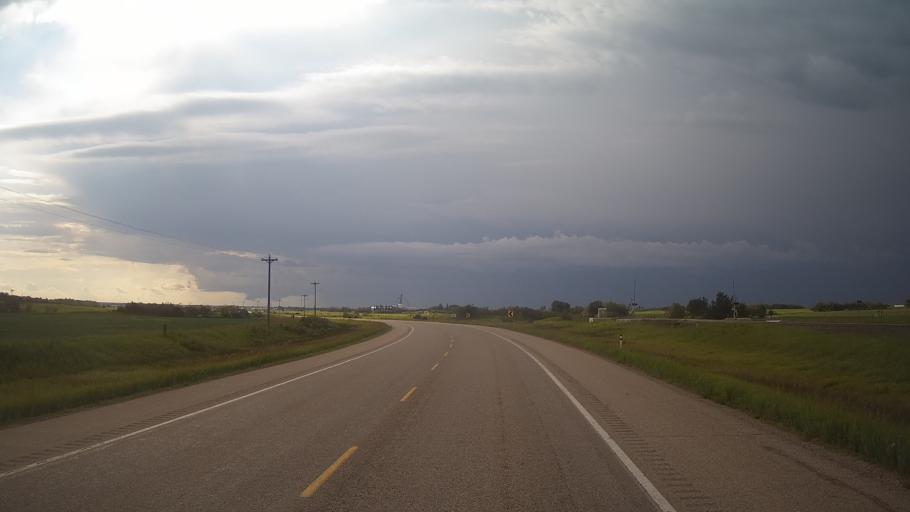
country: CA
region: Alberta
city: Vegreville
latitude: 53.2207
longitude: -112.2045
